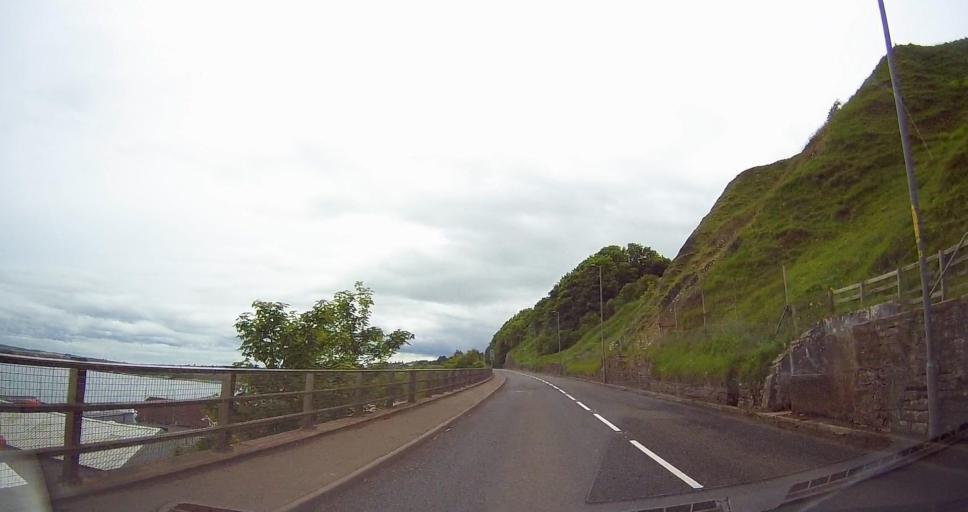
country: GB
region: Scotland
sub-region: Highland
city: Thurso
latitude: 58.6094
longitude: -3.5525
